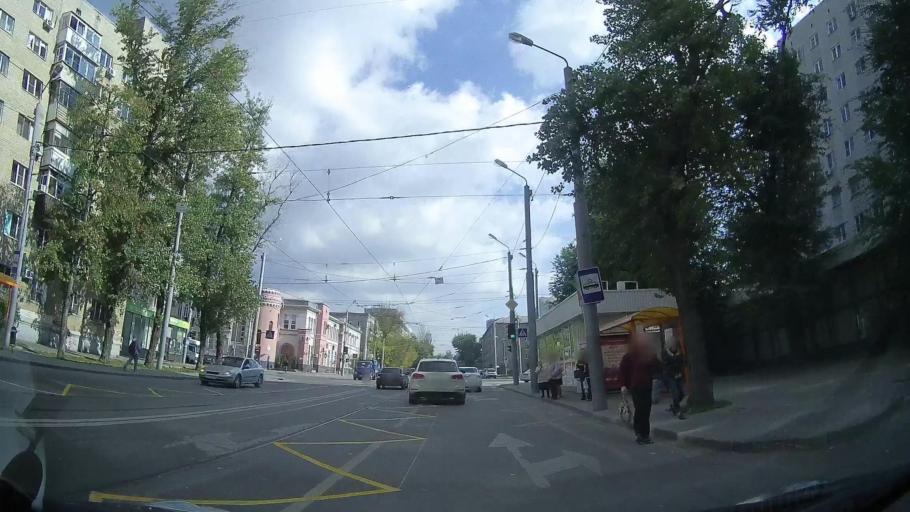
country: RU
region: Rostov
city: Rostov-na-Donu
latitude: 47.2319
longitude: 39.7397
